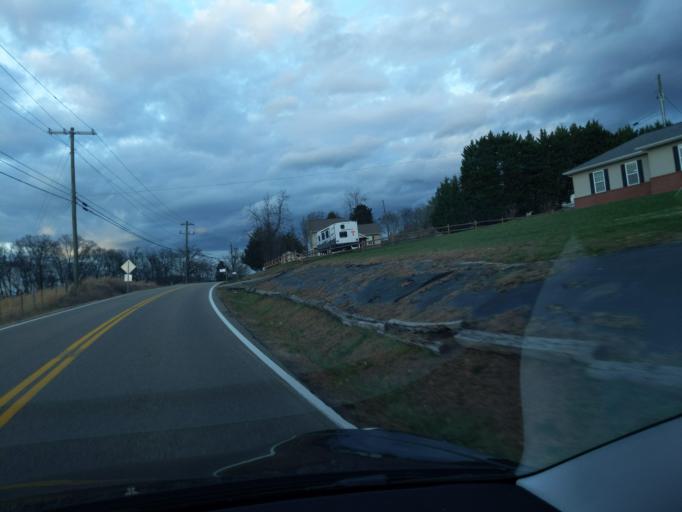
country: US
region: Tennessee
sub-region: Jefferson County
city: Dandridge
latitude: 36.0292
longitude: -83.4113
